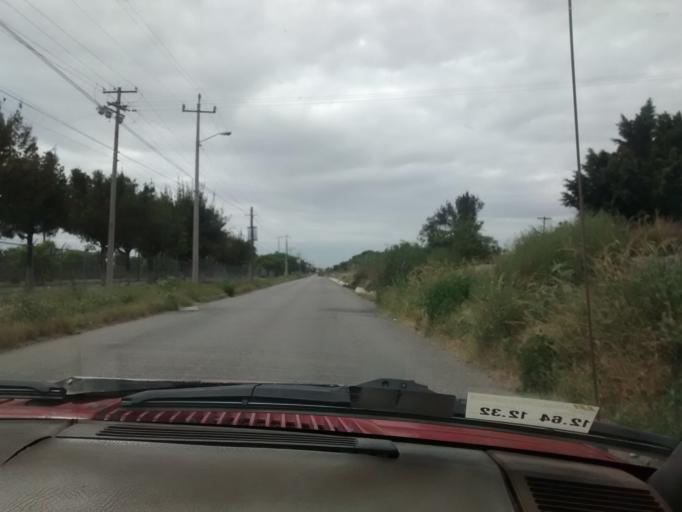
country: MX
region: Puebla
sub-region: Santiago Miahuatlan
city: San Jose Monte Chiquito
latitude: 18.4889
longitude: -97.4173
